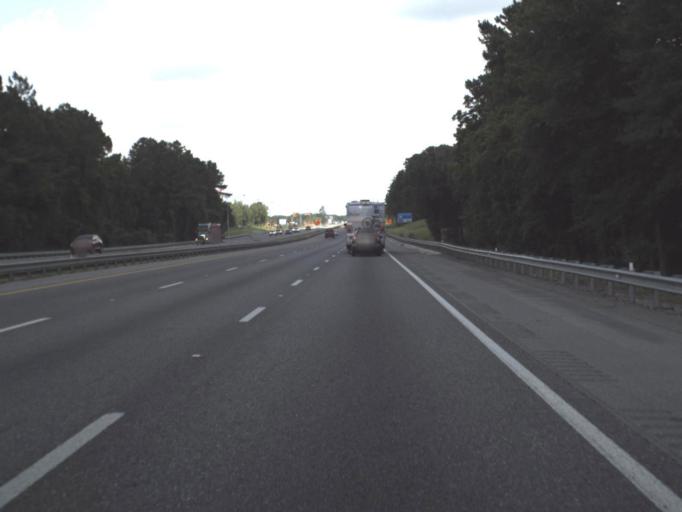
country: US
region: Florida
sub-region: Columbia County
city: Lake City
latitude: 30.1101
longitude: -82.6513
